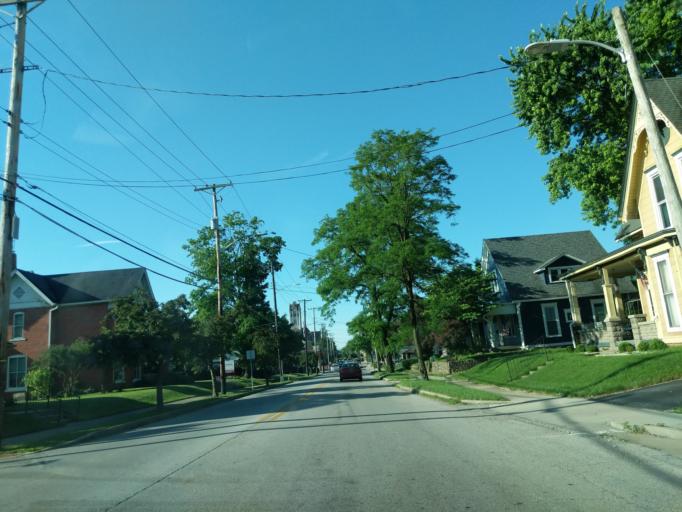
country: US
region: Indiana
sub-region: Hancock County
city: Greenfield
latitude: 39.7889
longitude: -85.7695
